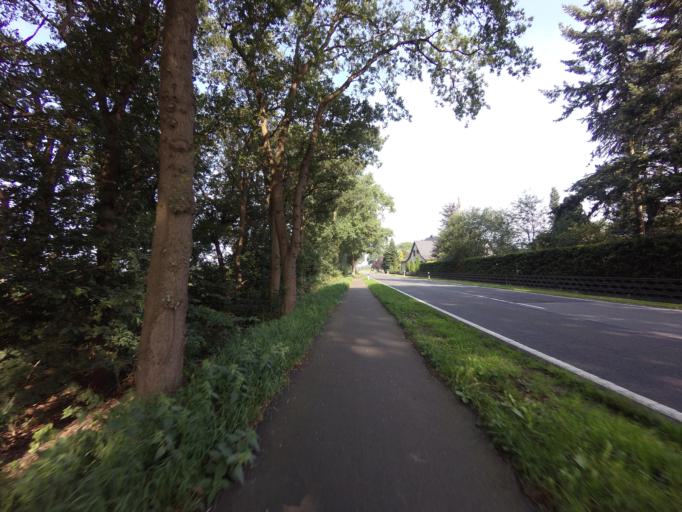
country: DE
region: Lower Saxony
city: Wielen
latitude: 52.5509
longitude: 6.6864
